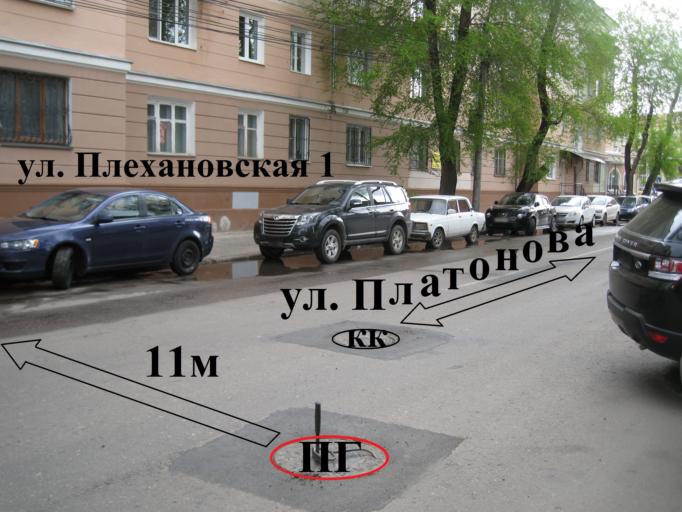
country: RU
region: Voronezj
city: Voronezh
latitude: 51.6575
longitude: 39.2032
